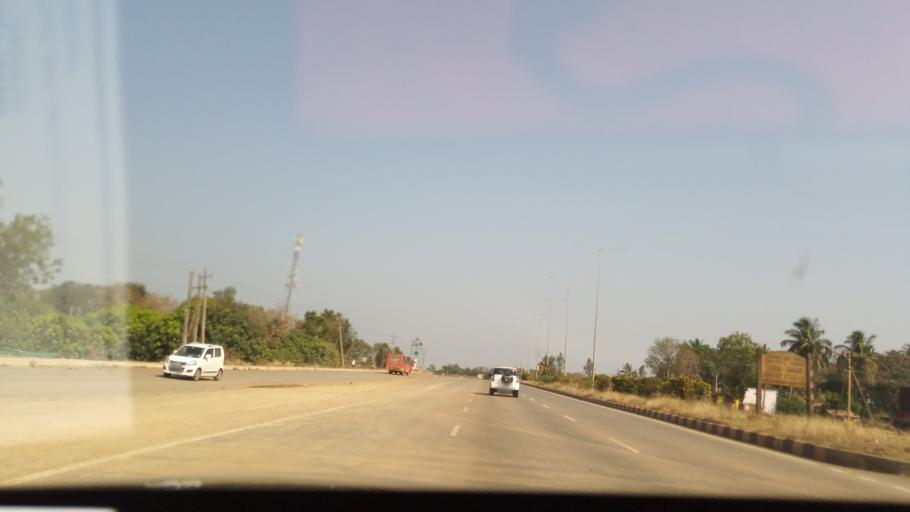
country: IN
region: Karnataka
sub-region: Dharwad
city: Kundgol
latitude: 15.1654
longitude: 75.1411
